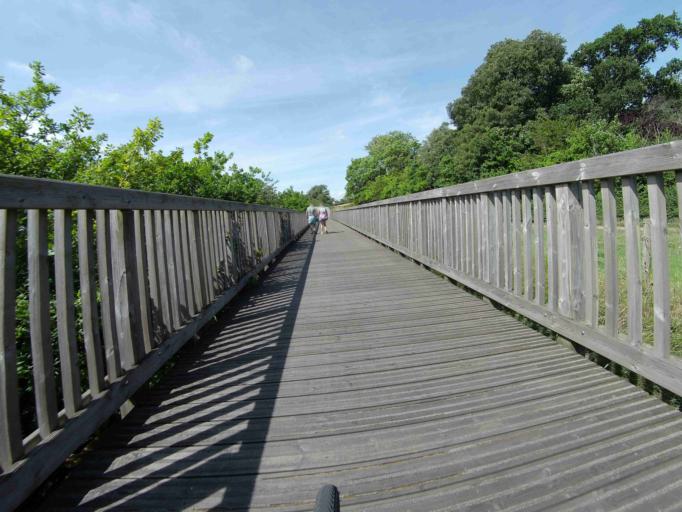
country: GB
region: England
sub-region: Devon
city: Starcross
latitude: 50.6567
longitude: -3.4358
